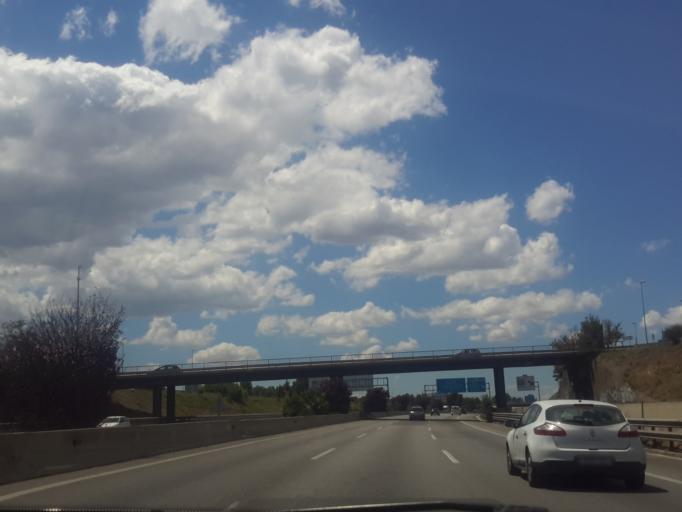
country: ES
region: Catalonia
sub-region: Provincia de Barcelona
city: Sant Cugat del Valles
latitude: 41.4884
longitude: 2.0841
